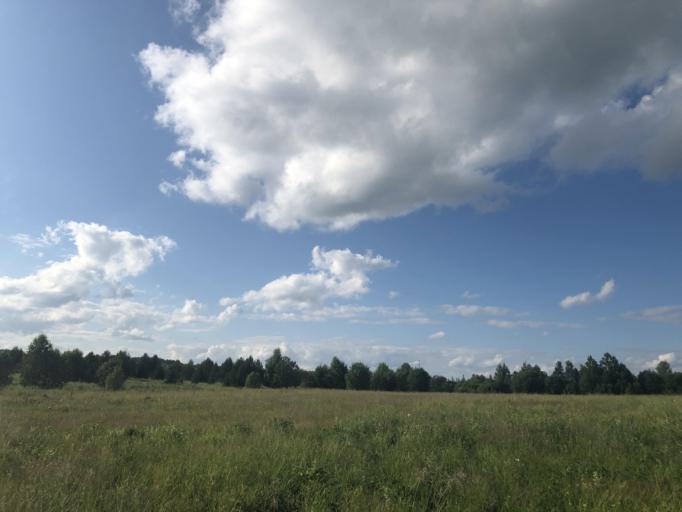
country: RU
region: Komi Republic
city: Vizinga
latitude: 61.2523
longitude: 50.5508
